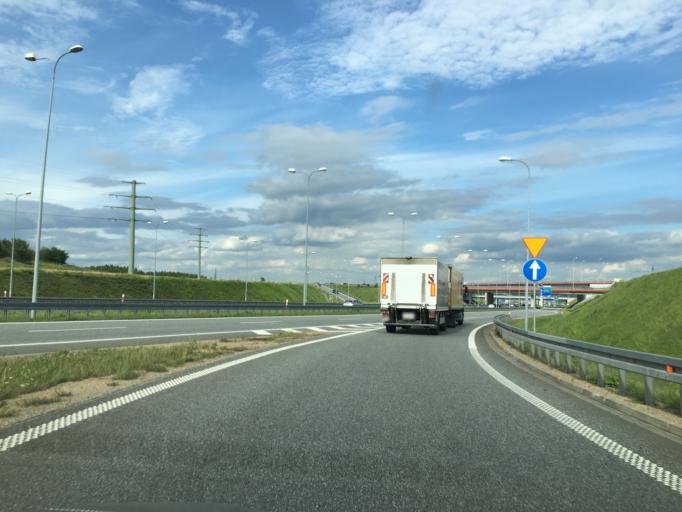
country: PL
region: Silesian Voivodeship
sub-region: Powiat gliwicki
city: Przyszowice
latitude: 50.2596
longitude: 18.7150
